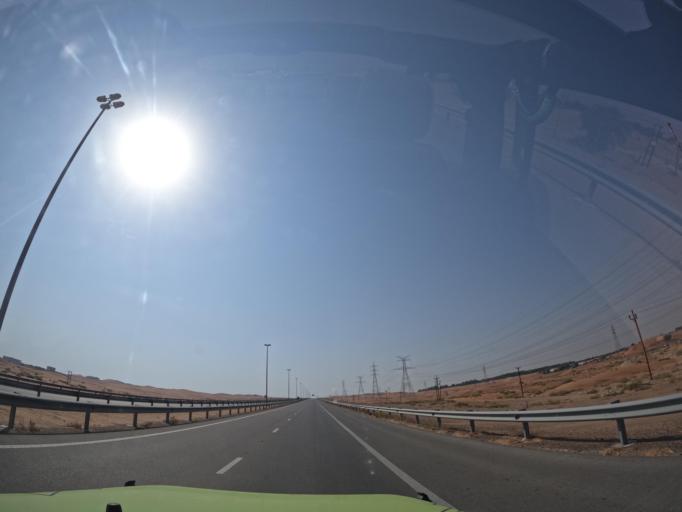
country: OM
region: Al Buraimi
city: Al Buraymi
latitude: 24.3558
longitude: 55.7341
